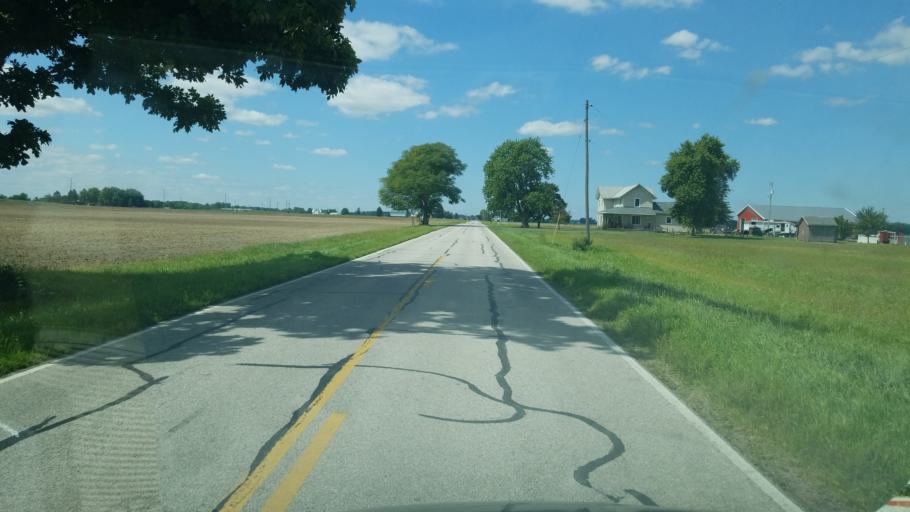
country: US
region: Ohio
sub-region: Fulton County
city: Delta
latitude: 41.6032
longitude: -83.9900
